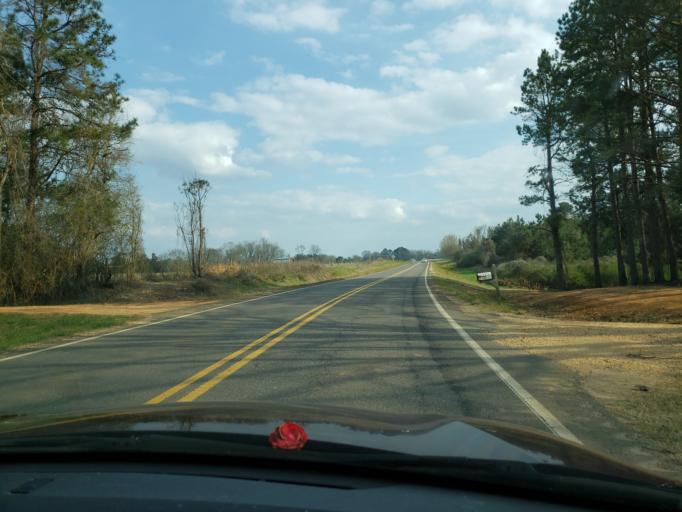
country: US
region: Alabama
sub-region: Hale County
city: Greensboro
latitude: 32.7203
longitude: -87.6217
